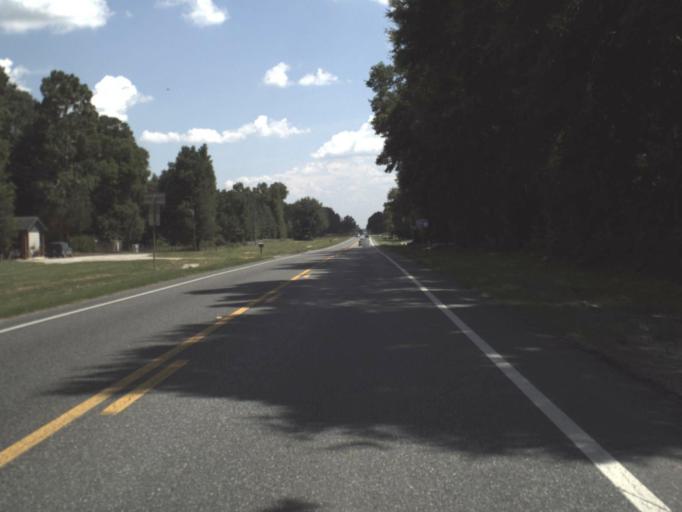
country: US
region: Florida
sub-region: Alachua County
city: High Springs
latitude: 29.9073
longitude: -82.6095
